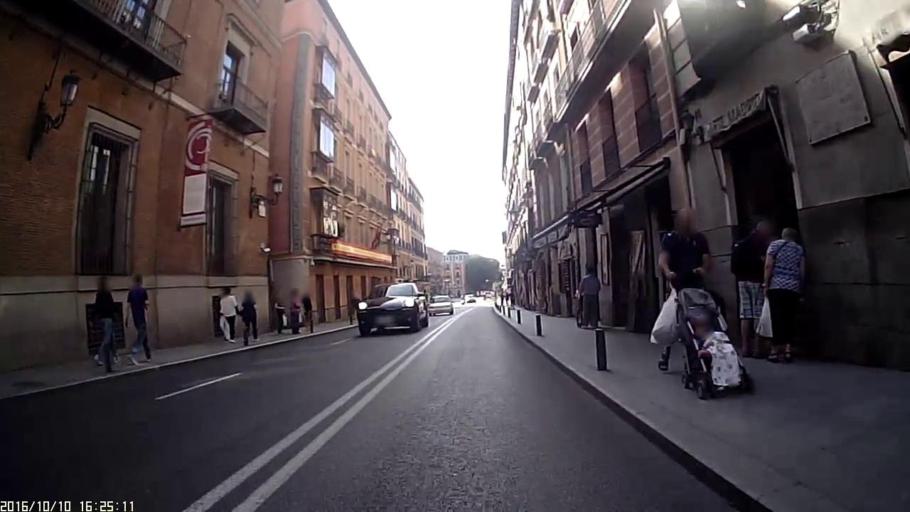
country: ES
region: Madrid
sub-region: Provincia de Madrid
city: Madrid
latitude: 40.4154
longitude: -3.7111
